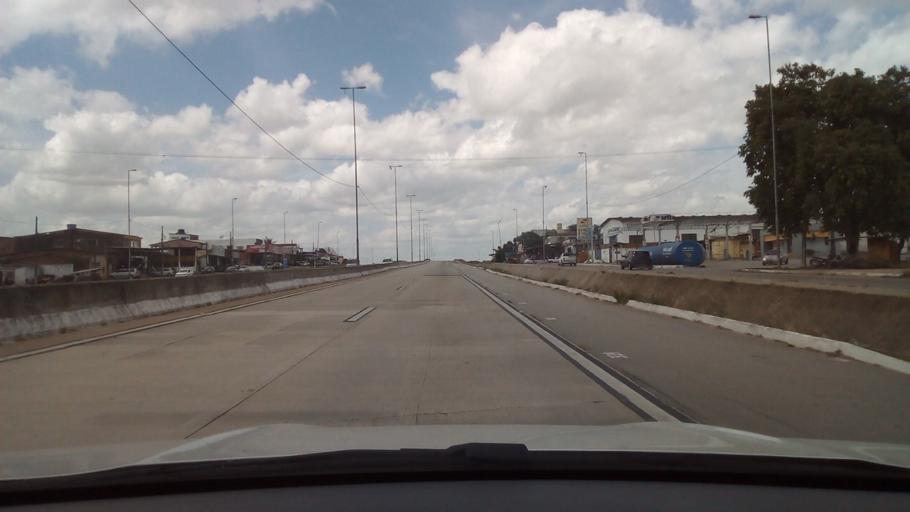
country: BR
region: Paraiba
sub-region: Mamanguape
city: Mamanguape
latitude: -6.8428
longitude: -35.1359
